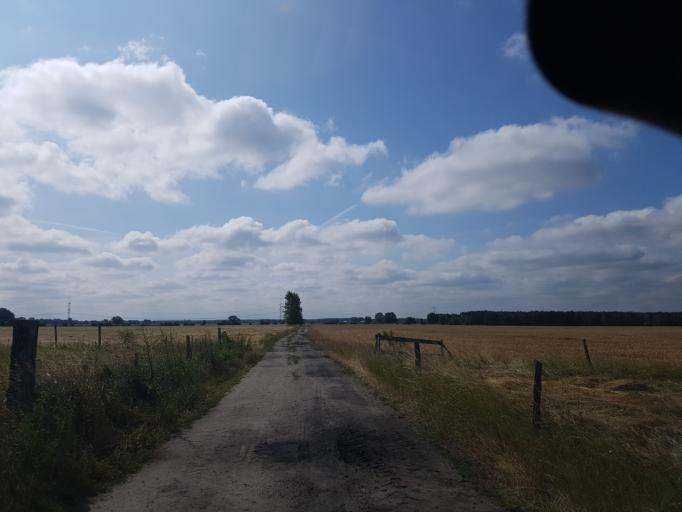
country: DE
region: Brandenburg
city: Schonborn
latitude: 51.5891
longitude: 13.5110
